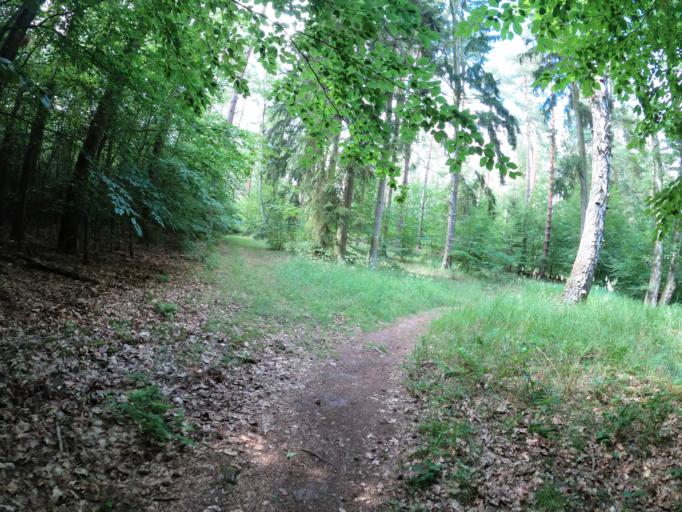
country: DE
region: Brandenburg
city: Angermunde
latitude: 53.0278
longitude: 13.9308
